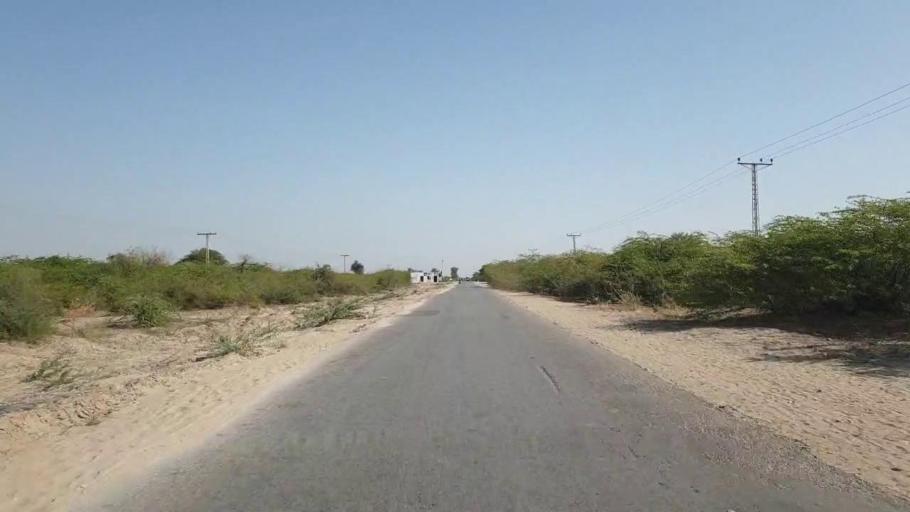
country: PK
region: Sindh
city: Chor
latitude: 25.4592
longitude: 69.7623
